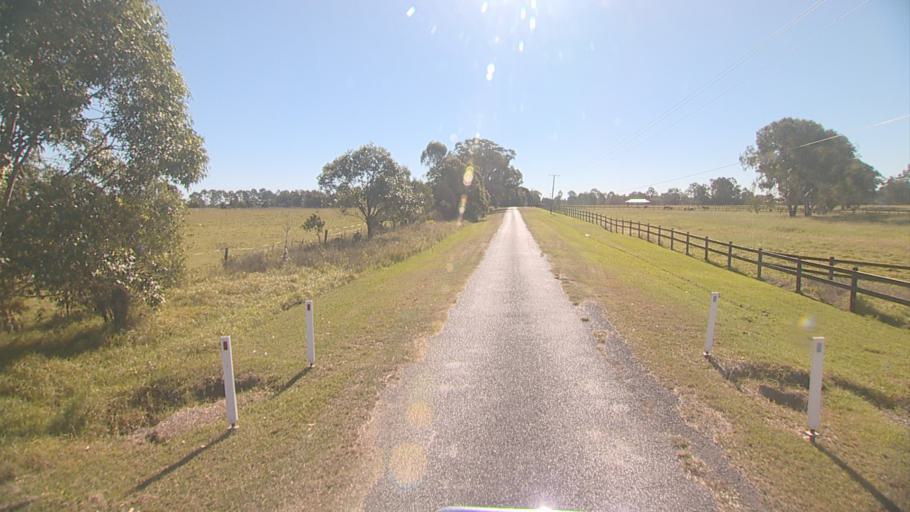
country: AU
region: Queensland
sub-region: Logan
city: Waterford West
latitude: -27.7058
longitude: 153.1309
